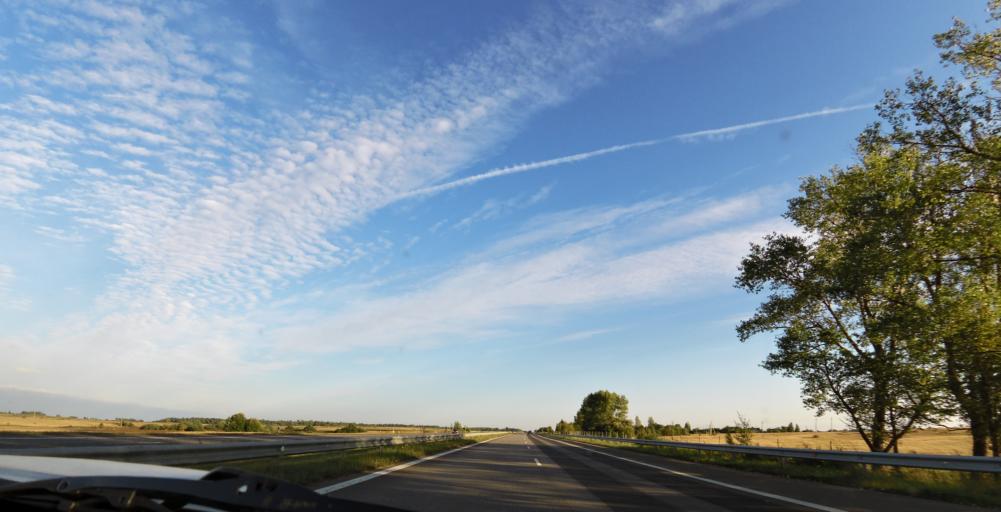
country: LT
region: Vilnius County
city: Ukmerge
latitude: 55.1543
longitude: 24.8223
